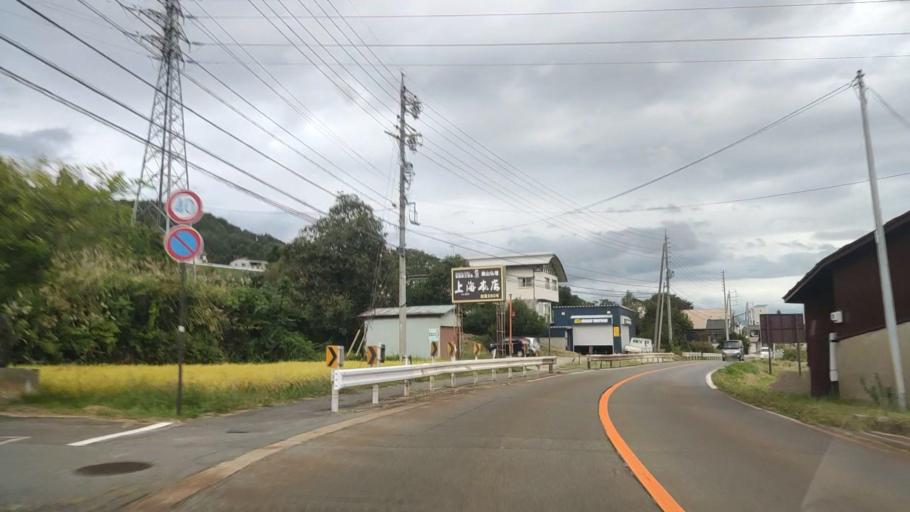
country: JP
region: Nagano
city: Iiyama
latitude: 36.8190
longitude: 138.3485
